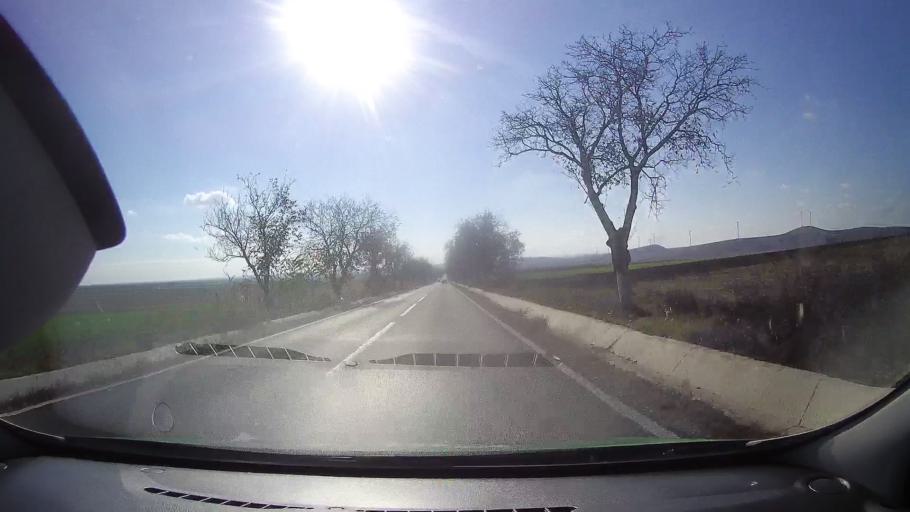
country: RO
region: Tulcea
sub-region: Comuna Ceamurlia de Jos
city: Ceamurlia de Jos
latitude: 44.8038
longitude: 28.6907
